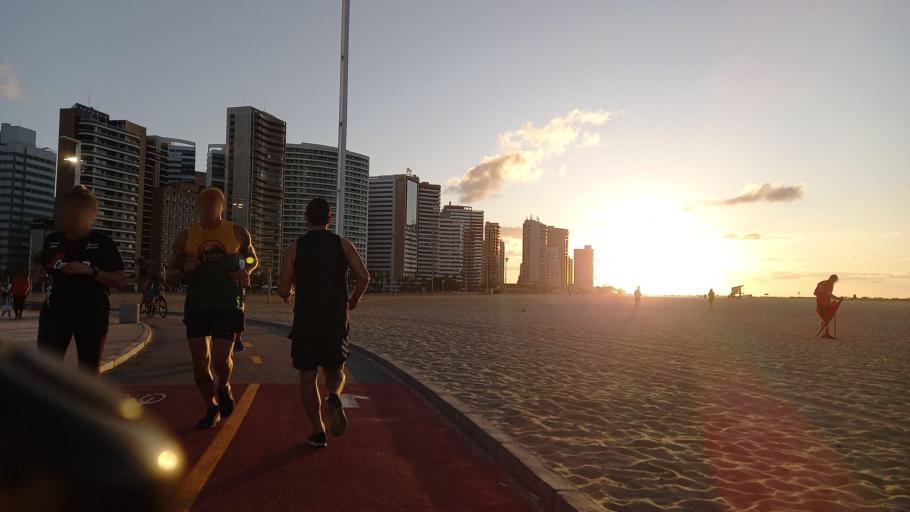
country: BR
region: Ceara
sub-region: Fortaleza
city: Fortaleza
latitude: -3.7223
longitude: -38.5051
